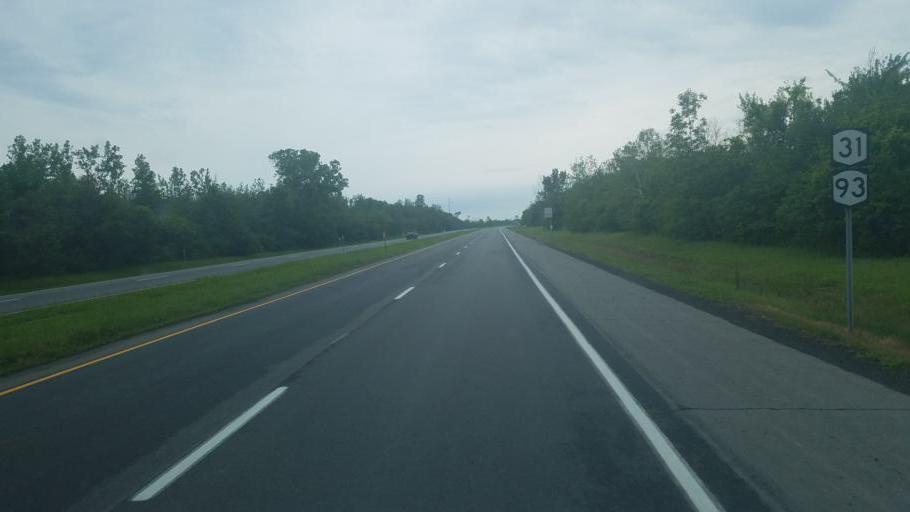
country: US
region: New York
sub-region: Niagara County
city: South Lockport
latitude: 43.1624
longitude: -78.7262
